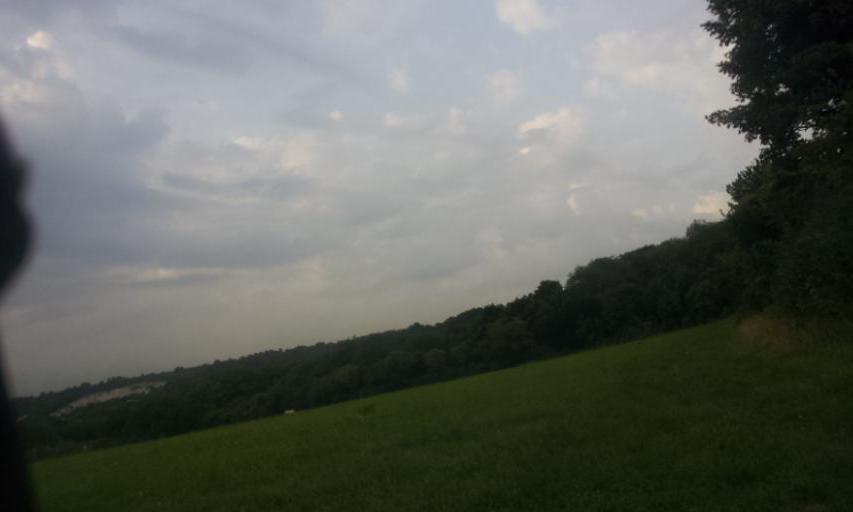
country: GB
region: England
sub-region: Kent
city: Aylesford
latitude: 51.3199
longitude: 0.5031
